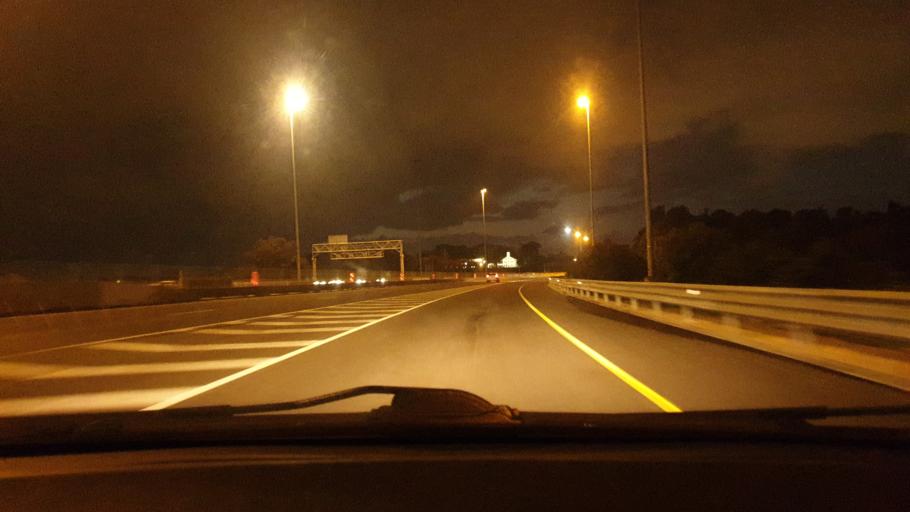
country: IL
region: Central District
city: Ramla
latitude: 31.9231
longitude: 34.8358
